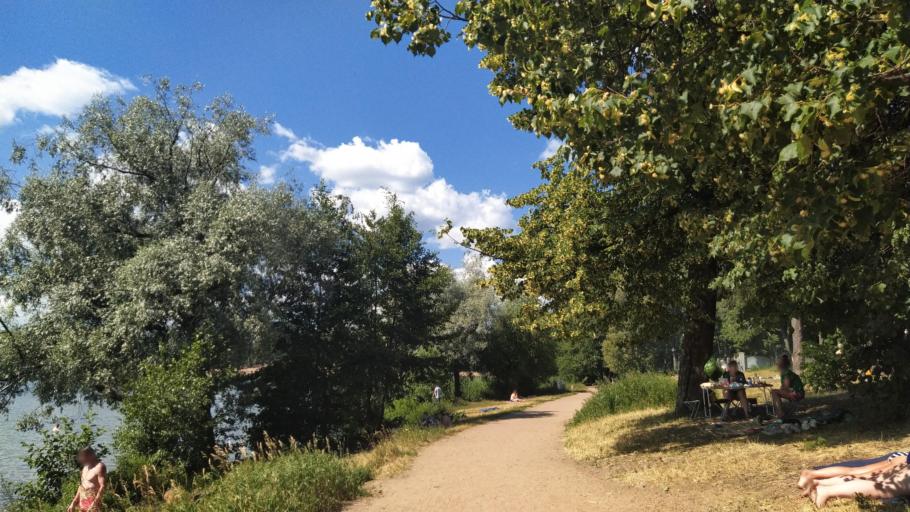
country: RU
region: St.-Petersburg
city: Ozerki
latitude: 60.0380
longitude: 30.3158
